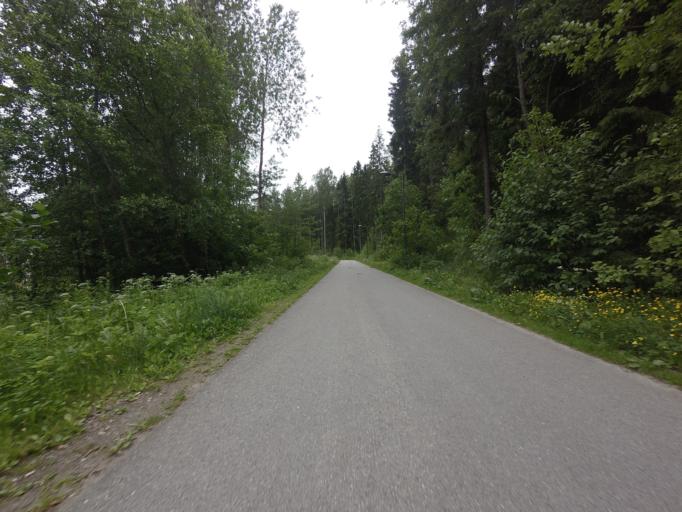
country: FI
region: Uusimaa
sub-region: Helsinki
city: Kauniainen
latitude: 60.1835
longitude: 24.7378
